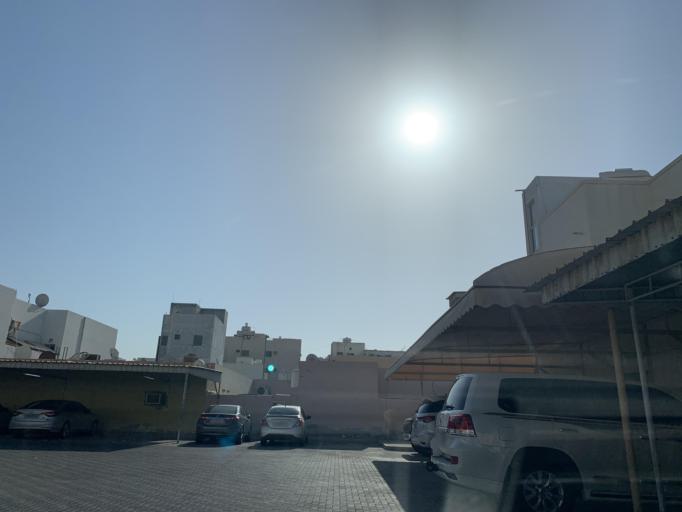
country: BH
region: Muharraq
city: Al Muharraq
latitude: 26.2652
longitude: 50.6062
